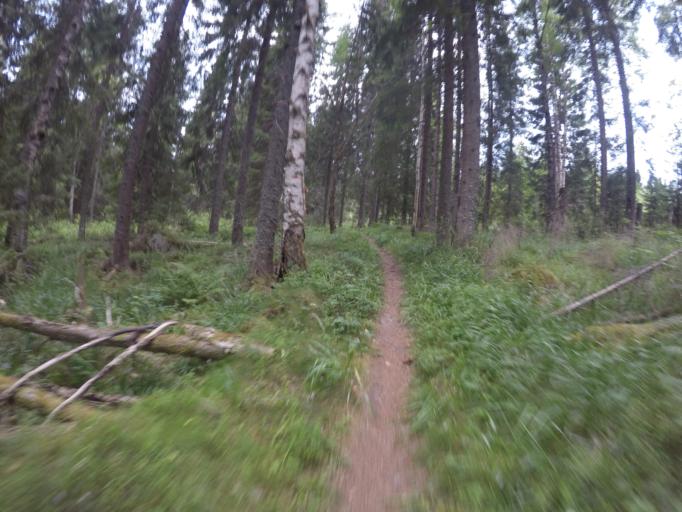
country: SE
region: Vaermland
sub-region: Filipstads Kommun
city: Lesjofors
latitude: 60.1582
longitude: 14.3917
